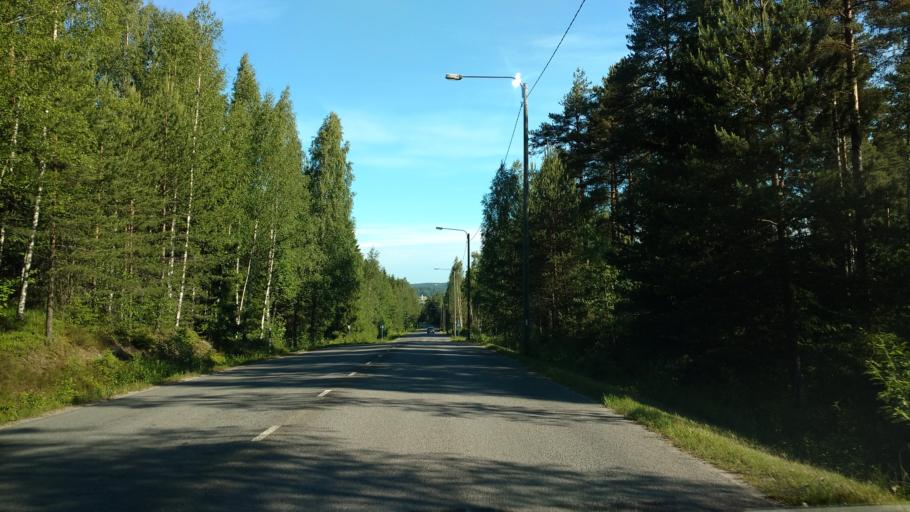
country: FI
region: Varsinais-Suomi
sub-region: Salo
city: Salo
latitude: 60.3947
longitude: 23.1786
